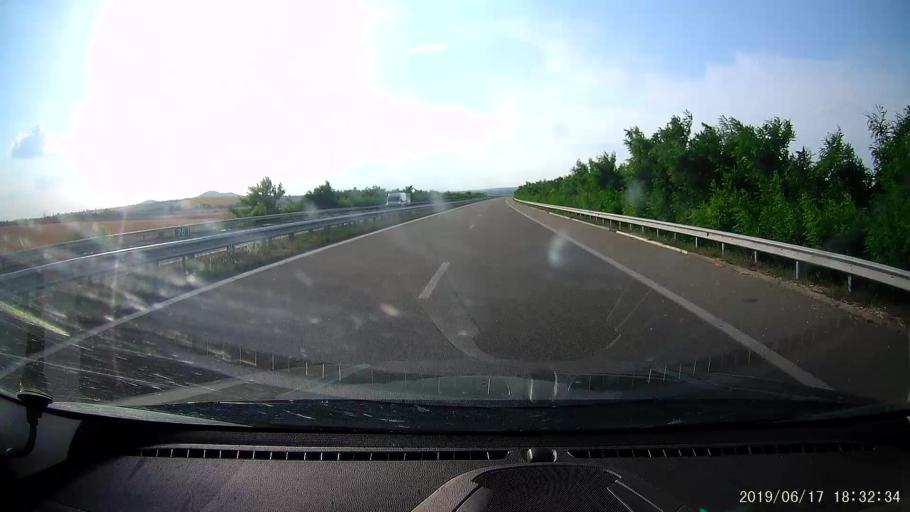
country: BG
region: Khaskovo
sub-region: Obshtina Dimitrovgrad
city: Dimitrovgrad
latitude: 42.0619
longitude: 25.4759
